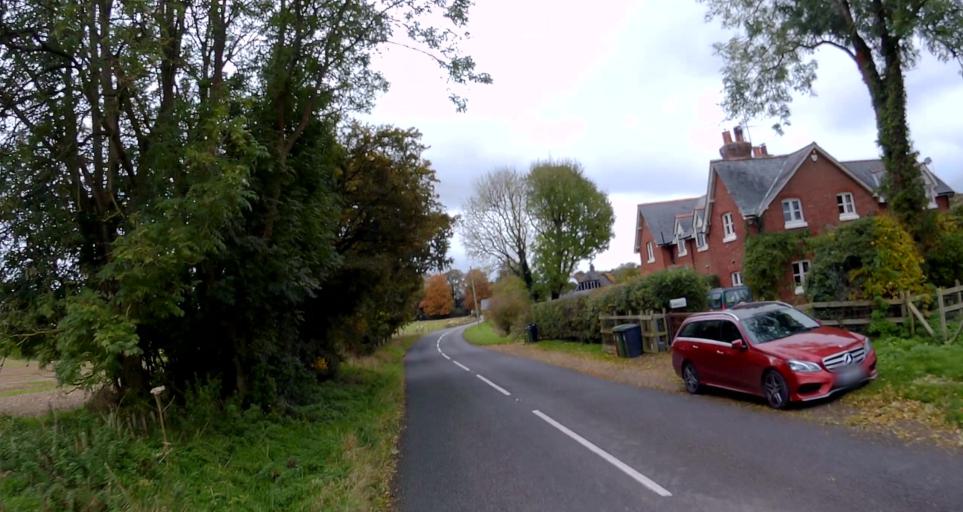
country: GB
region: England
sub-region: Hampshire
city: Four Marks
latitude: 51.1594
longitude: -1.1488
